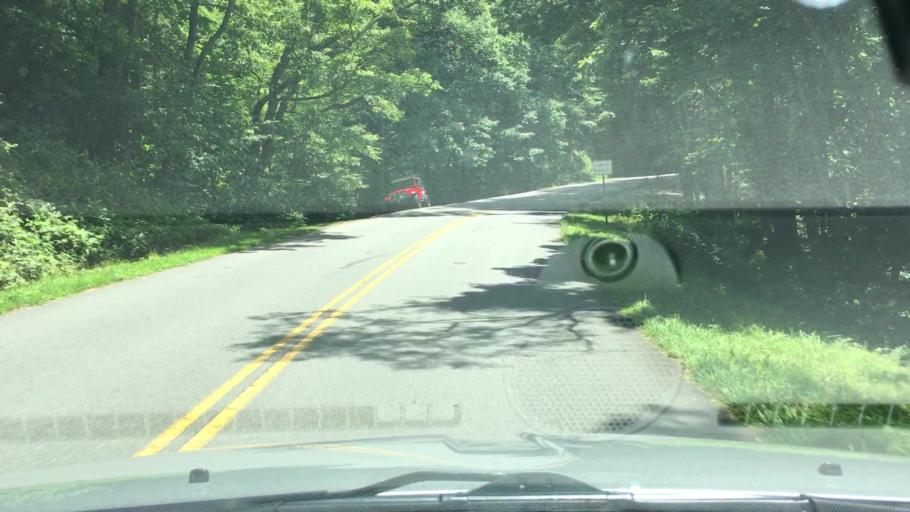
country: US
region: North Carolina
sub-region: Buncombe County
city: Swannanoa
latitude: 35.6661
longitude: -82.4622
